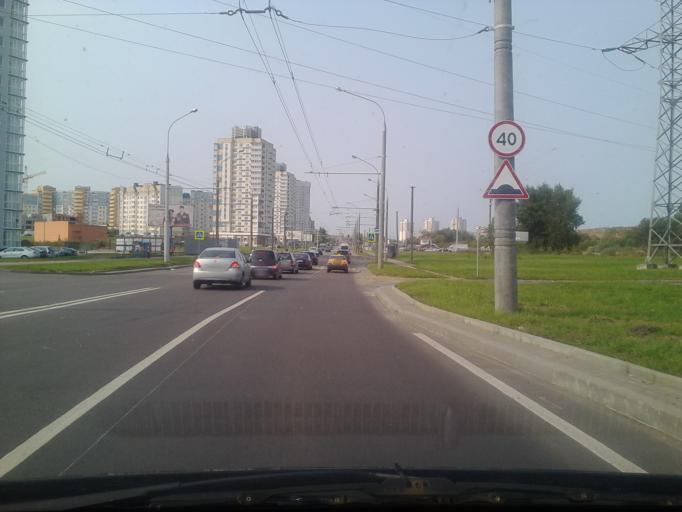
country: BY
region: Minsk
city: Novoye Medvezhino
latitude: 53.8759
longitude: 27.4620
